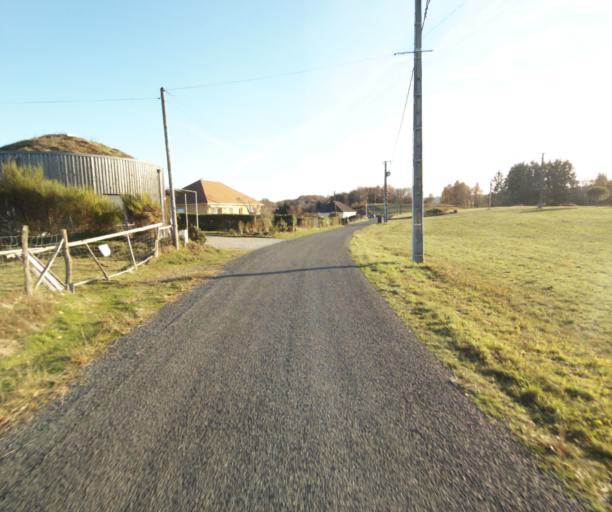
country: FR
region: Limousin
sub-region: Departement de la Correze
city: Laguenne
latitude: 45.2293
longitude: 1.8014
